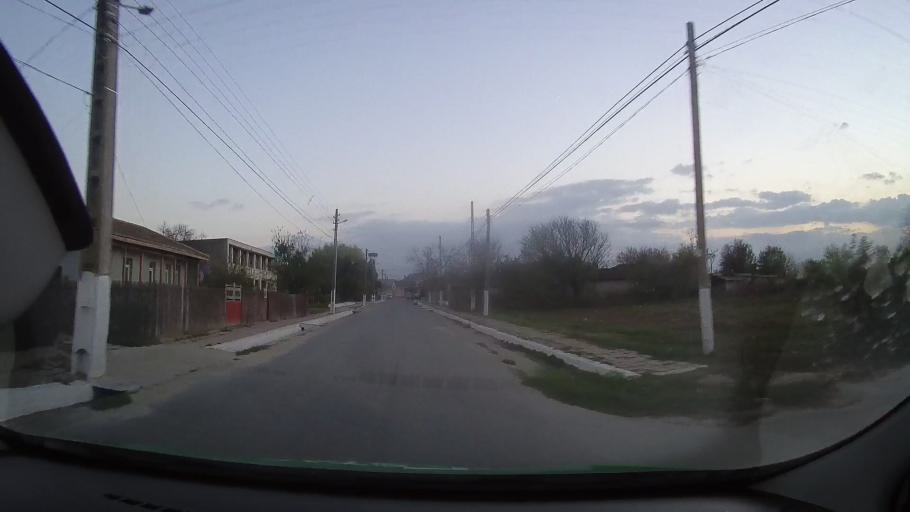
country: RO
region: Constanta
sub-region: Comuna Oltina
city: Oltina
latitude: 44.1668
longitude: 27.6648
